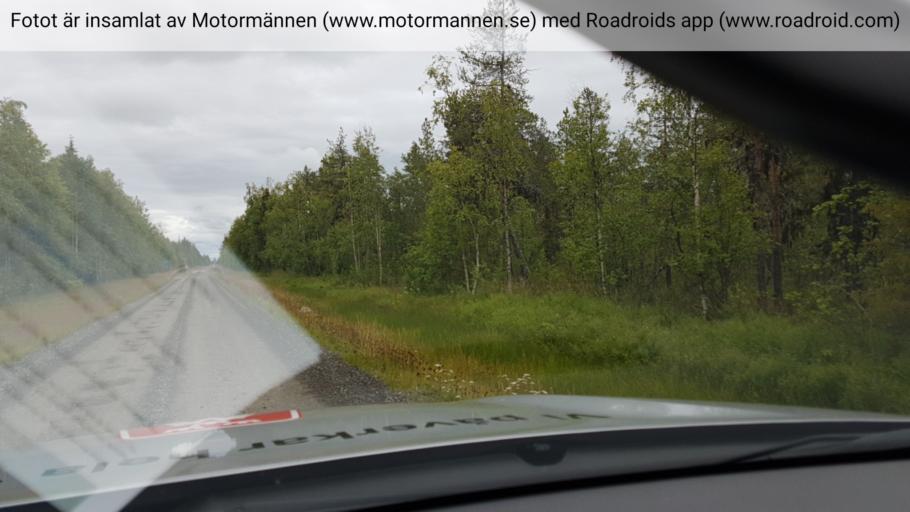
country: SE
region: Norrbotten
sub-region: Pajala Kommun
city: Pajala
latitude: 67.0876
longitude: 22.7619
